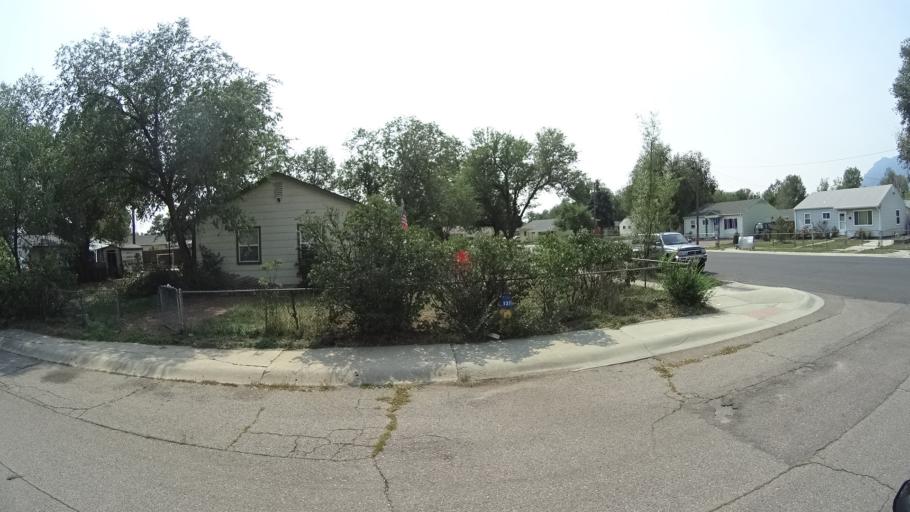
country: US
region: Colorado
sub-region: El Paso County
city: Colorado Springs
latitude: 38.8012
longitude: -104.8059
